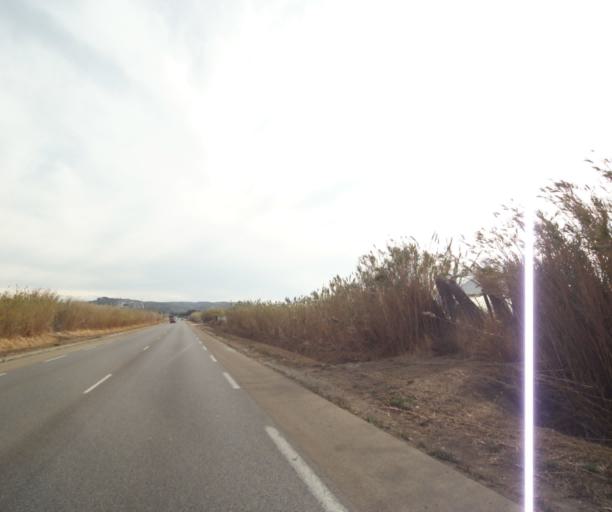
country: FR
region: Provence-Alpes-Cote d'Azur
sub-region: Departement des Bouches-du-Rhone
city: Gignac-la-Nerthe
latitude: 43.3896
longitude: 5.2109
